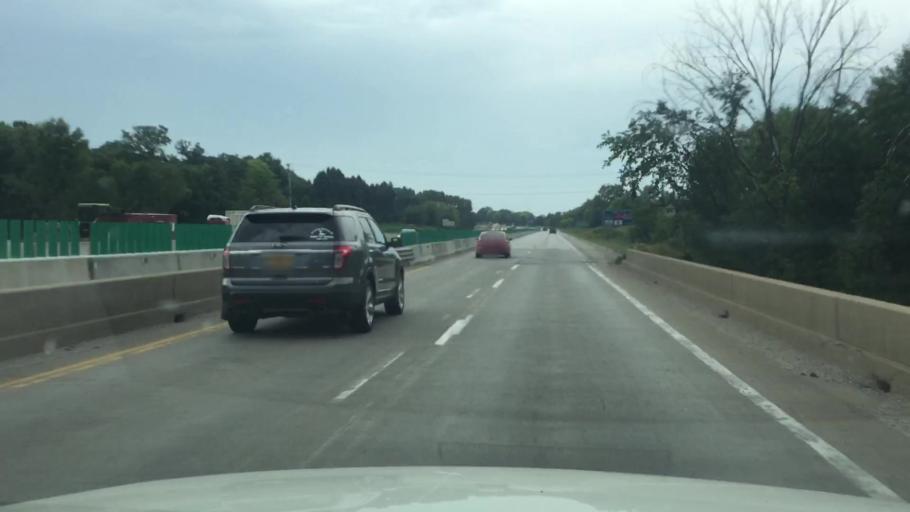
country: US
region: Iowa
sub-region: Polk County
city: Ankeny
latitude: 41.7474
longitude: -93.5754
